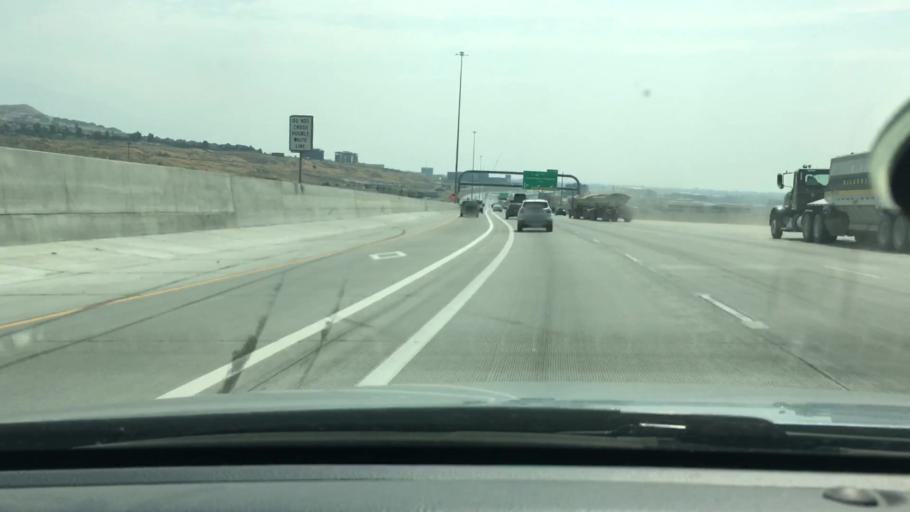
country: US
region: Utah
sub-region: Salt Lake County
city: Bluffdale
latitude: 40.4478
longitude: -111.9109
